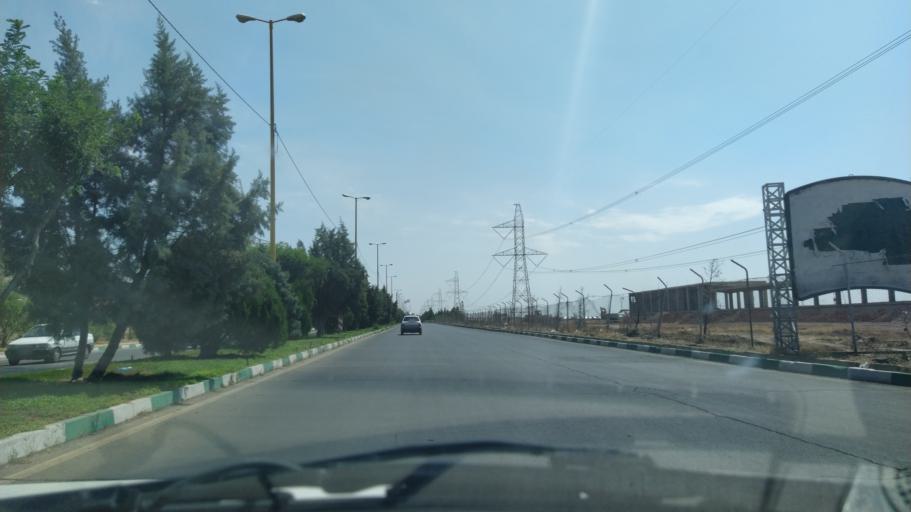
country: IR
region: Tehran
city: Robat Karim
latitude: 35.4644
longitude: 50.9762
